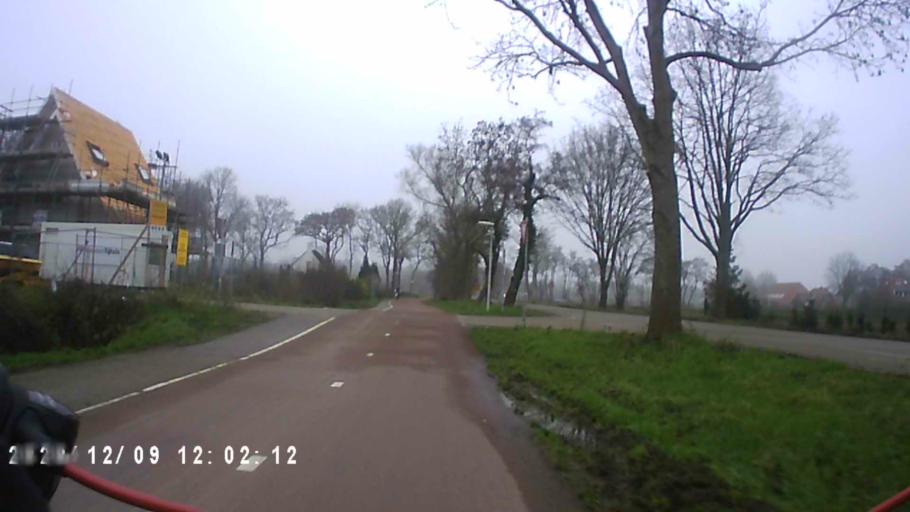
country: NL
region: Groningen
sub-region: Gemeente Haren
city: Haren
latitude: 53.1868
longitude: 6.5990
